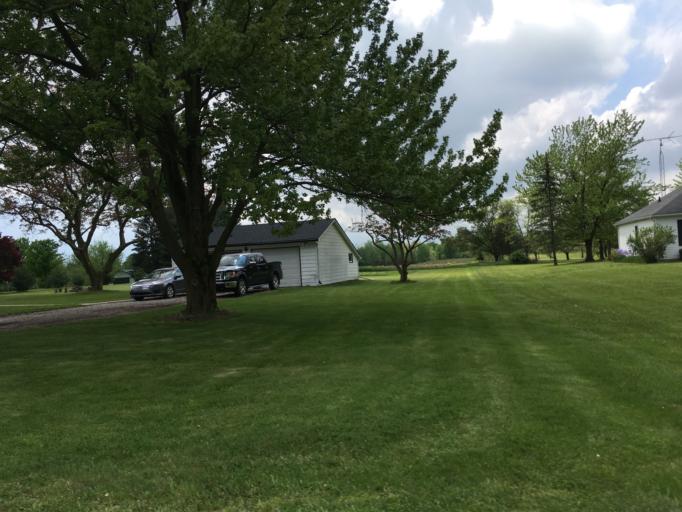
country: US
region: Michigan
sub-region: Washtenaw County
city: Saline
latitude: 42.1639
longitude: -83.8931
